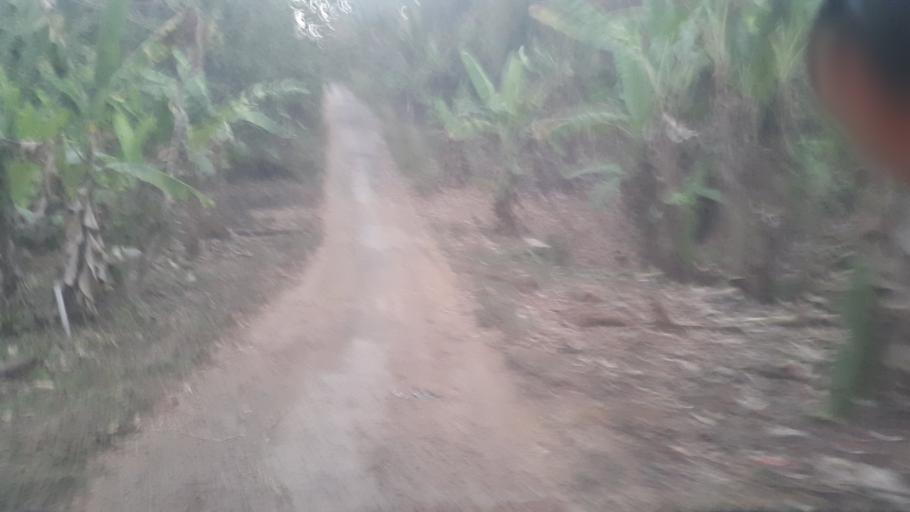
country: ID
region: West Java
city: Bojonggaling
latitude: -6.9669
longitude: 106.6041
